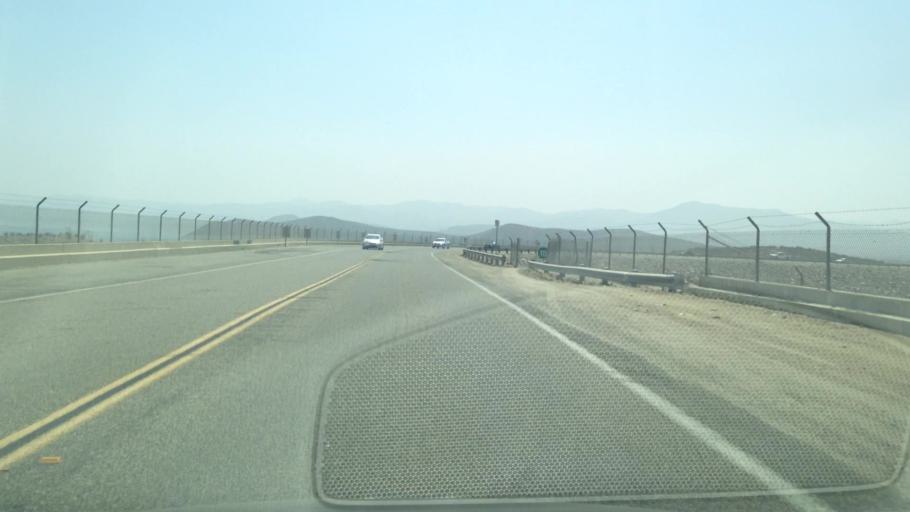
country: US
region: California
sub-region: Riverside County
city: El Cerrito
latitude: 33.8420
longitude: -117.4627
